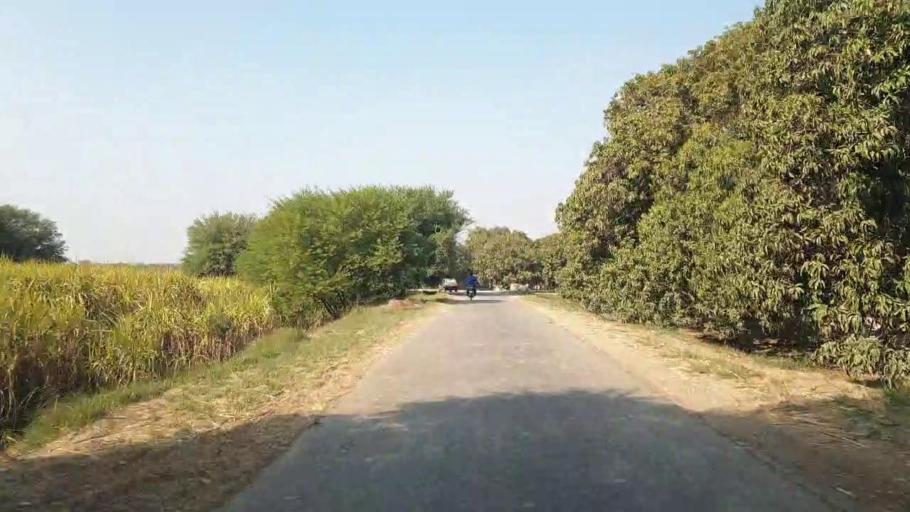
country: PK
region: Sindh
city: Mirwah Gorchani
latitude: 25.3786
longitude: 68.9511
